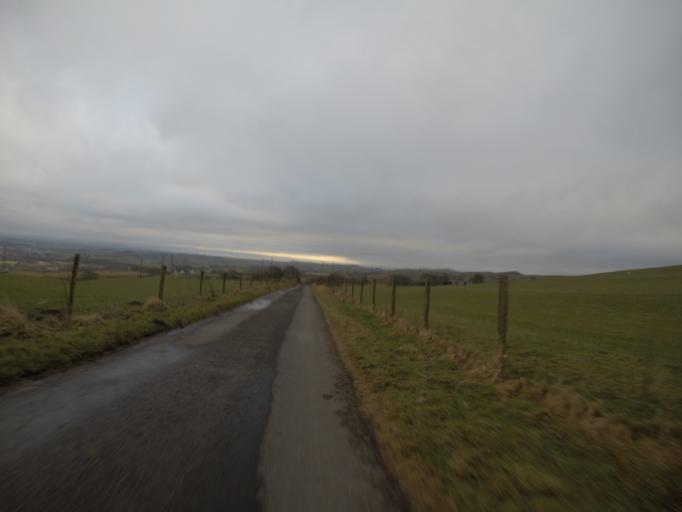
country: GB
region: Scotland
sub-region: North Ayrshire
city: Dalry
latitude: 55.7274
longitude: -4.7637
